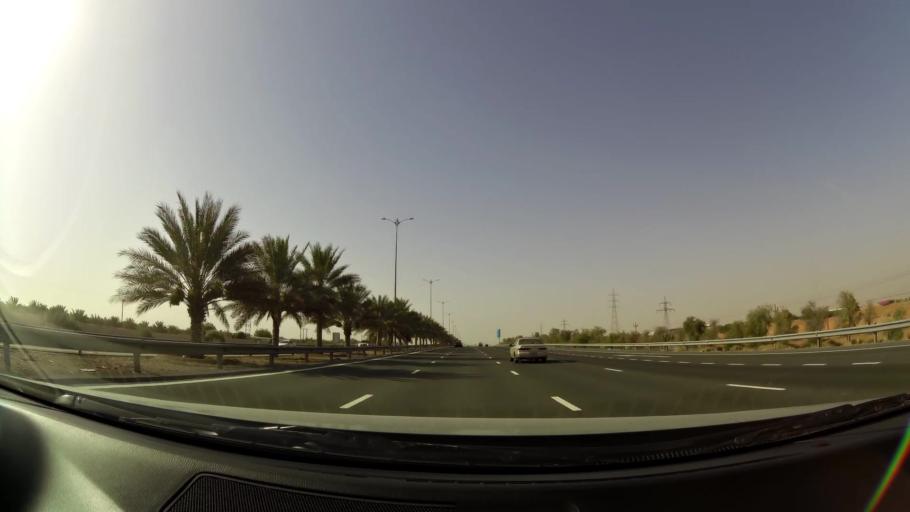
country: OM
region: Al Buraimi
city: Al Buraymi
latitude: 24.4767
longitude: 55.7758
